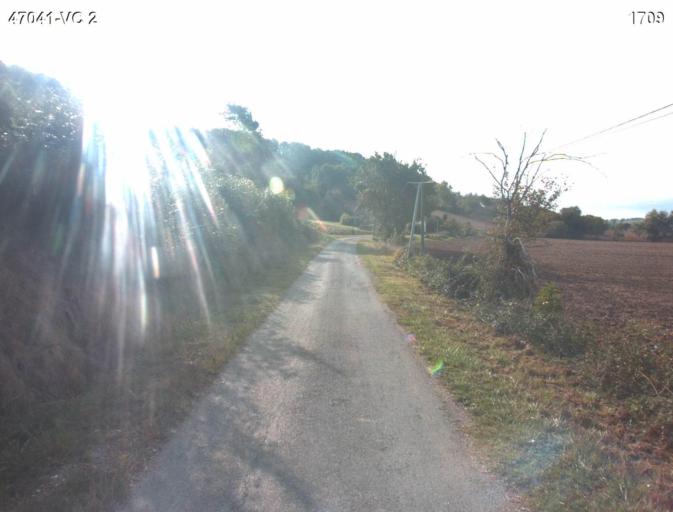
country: FR
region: Aquitaine
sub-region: Departement du Lot-et-Garonne
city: Port-Sainte-Marie
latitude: 44.1883
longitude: 0.4178
